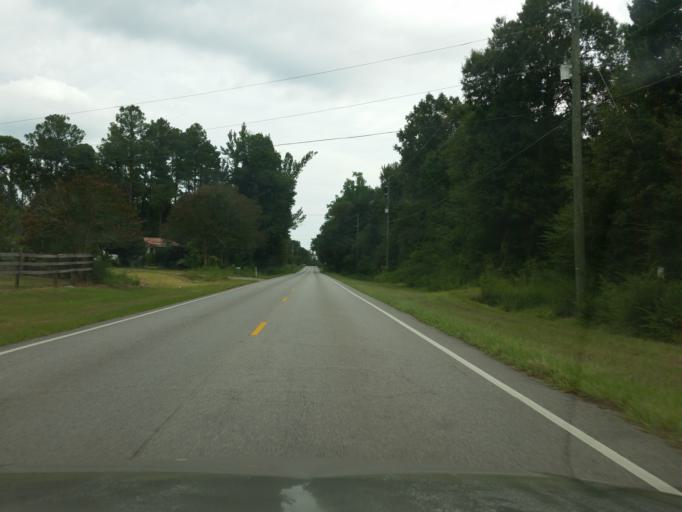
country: US
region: Florida
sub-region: Escambia County
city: Molino
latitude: 30.6873
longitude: -87.3259
